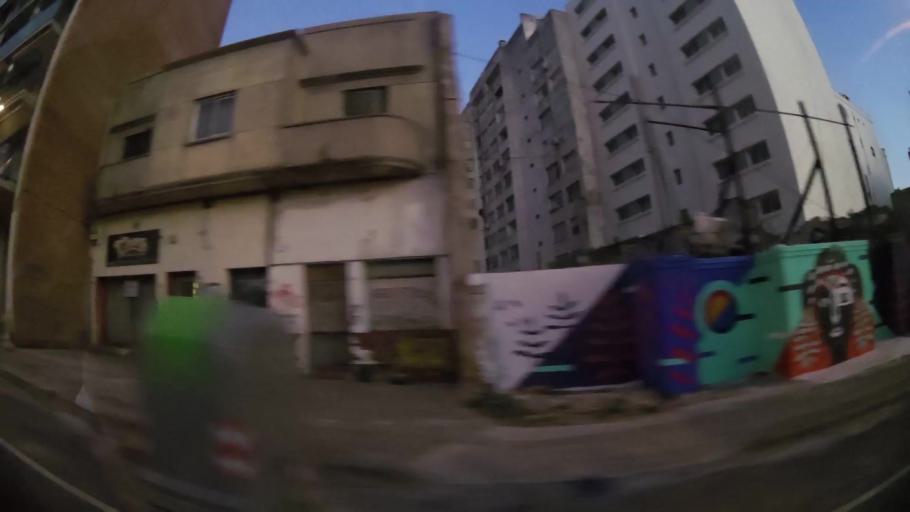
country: UY
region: Montevideo
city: Montevideo
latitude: -34.9090
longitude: -56.2000
